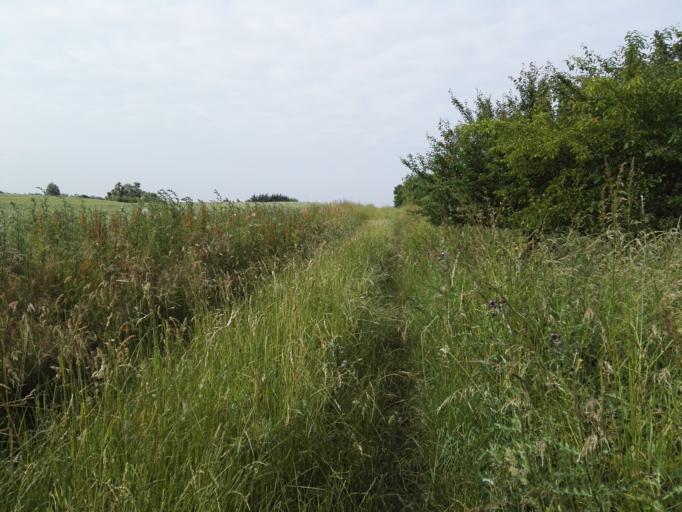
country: DK
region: Zealand
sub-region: Roskilde Kommune
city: Jyllinge
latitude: 55.7861
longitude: 12.0870
